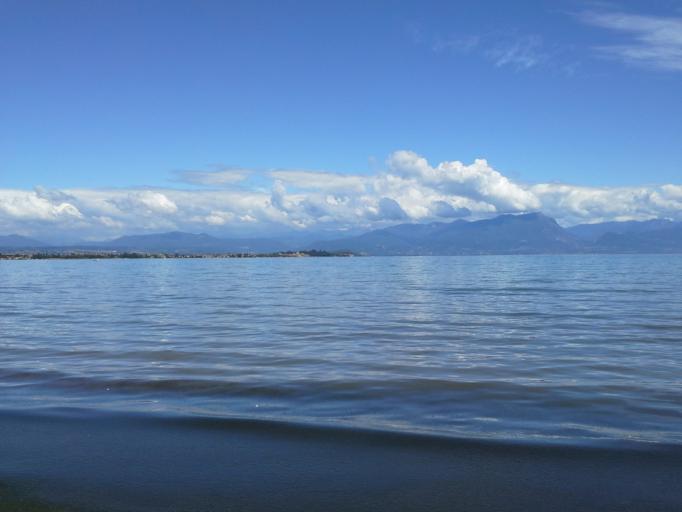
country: IT
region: Lombardy
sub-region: Provincia di Brescia
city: San Martino della Battaglia
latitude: 45.4612
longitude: 10.6323
